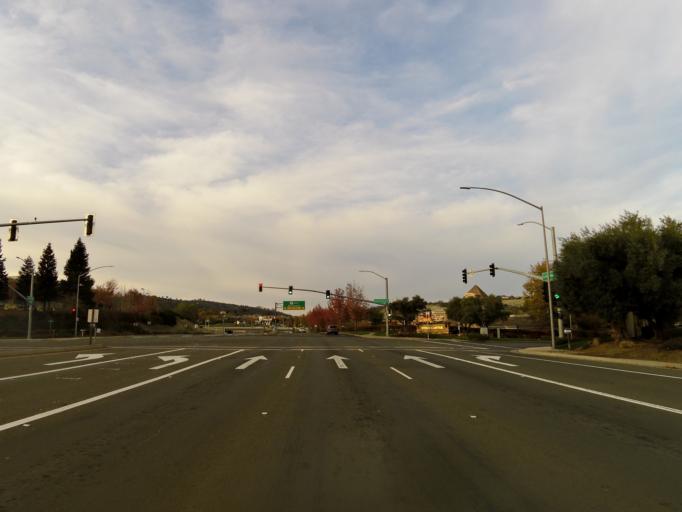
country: US
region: California
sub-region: El Dorado County
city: El Dorado Hills
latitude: 38.6494
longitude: -121.0687
